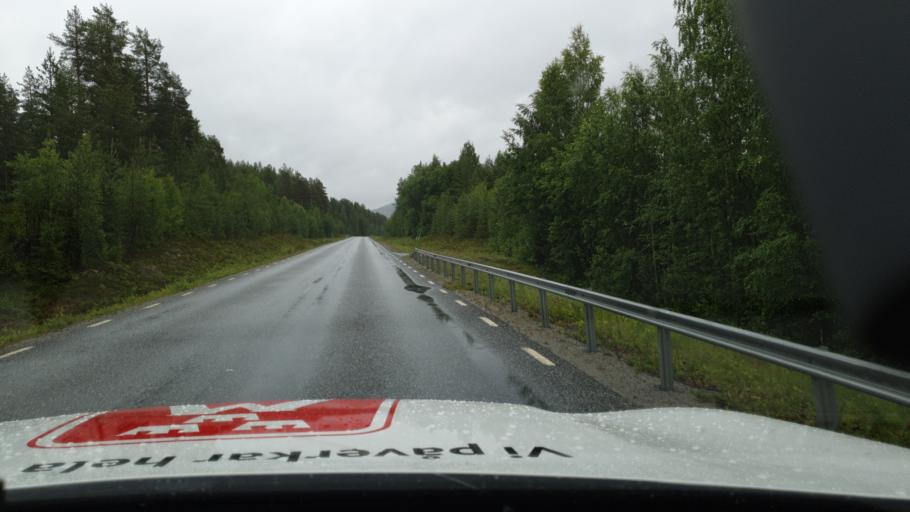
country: SE
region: Vaesterbotten
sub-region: Asele Kommun
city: Asele
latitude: 64.3349
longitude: 17.0518
